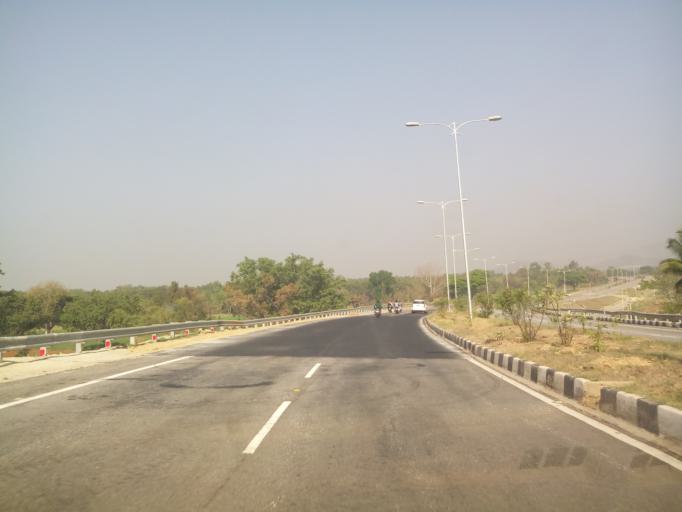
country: IN
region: Karnataka
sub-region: Tumkur
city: Kunigal
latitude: 13.0003
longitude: 77.0208
